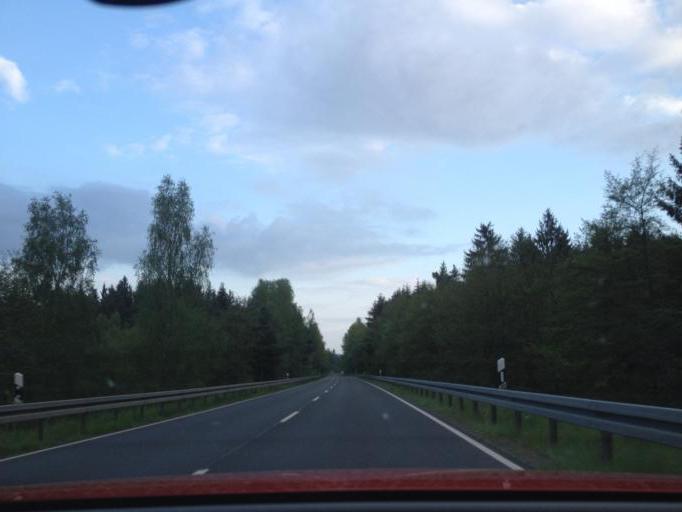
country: DE
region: Bavaria
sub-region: Upper Palatinate
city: Kohlberg
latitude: 49.5834
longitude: 11.9932
